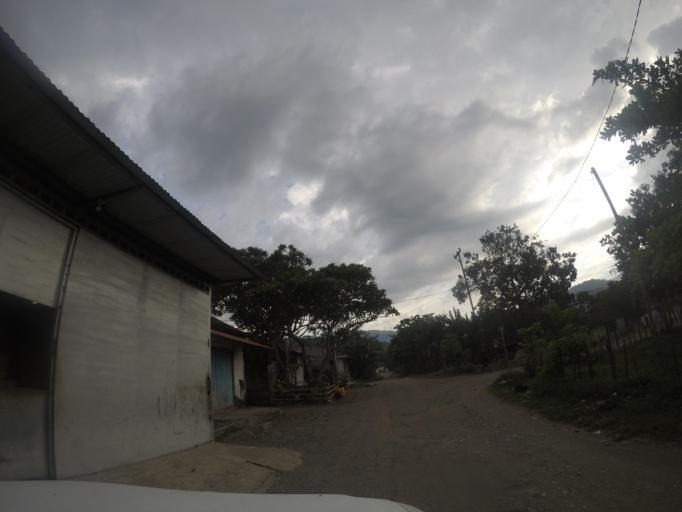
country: TL
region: Ermera
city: Gleno
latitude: -8.7231
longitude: 125.4373
